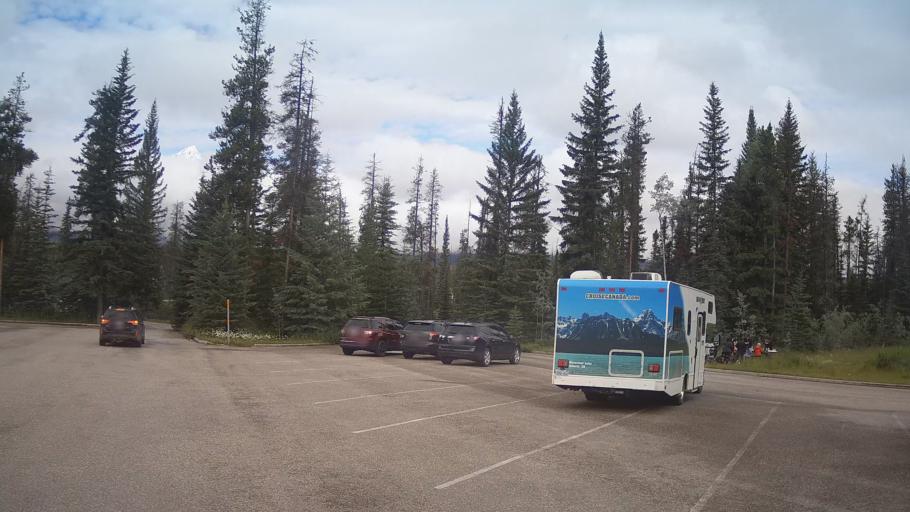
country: CA
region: Alberta
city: Jasper Park Lodge
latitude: 52.6657
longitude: -117.8827
